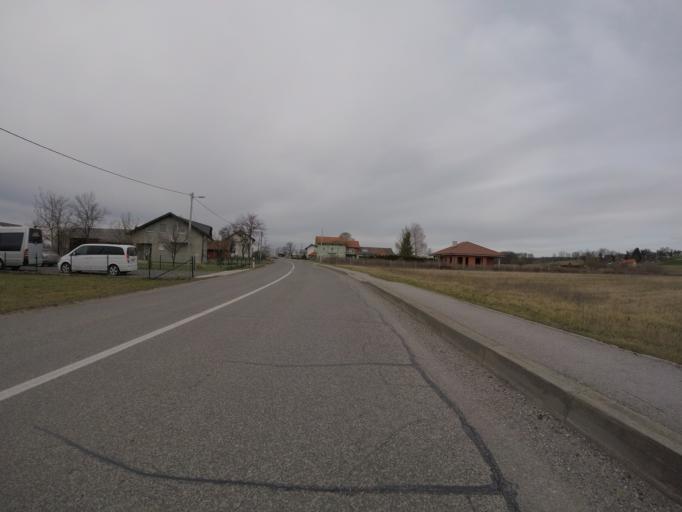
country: HR
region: Grad Zagreb
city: Horvati
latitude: 45.5773
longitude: 15.8608
